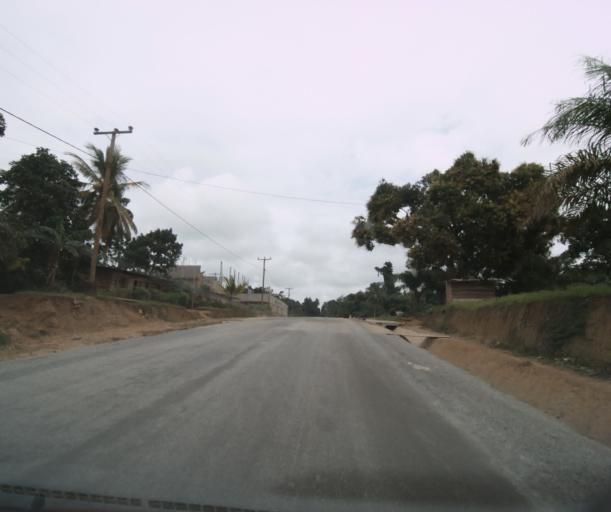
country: CM
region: South Province
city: Kribi
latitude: 2.9070
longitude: 9.9060
